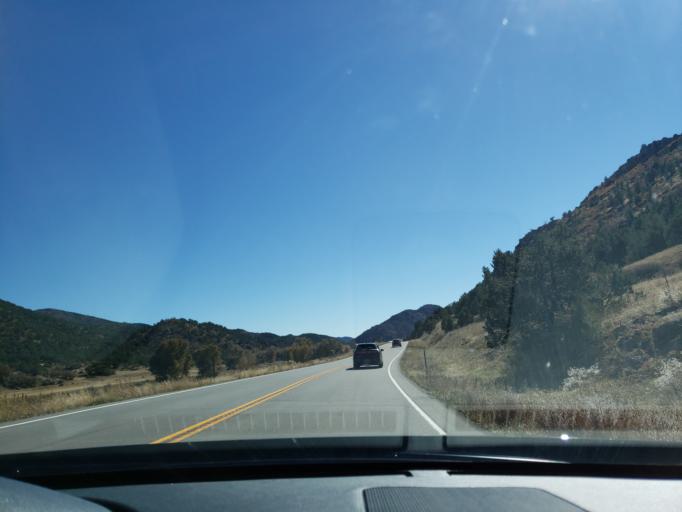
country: US
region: Colorado
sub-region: Fremont County
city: Canon City
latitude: 38.6020
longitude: -105.4308
